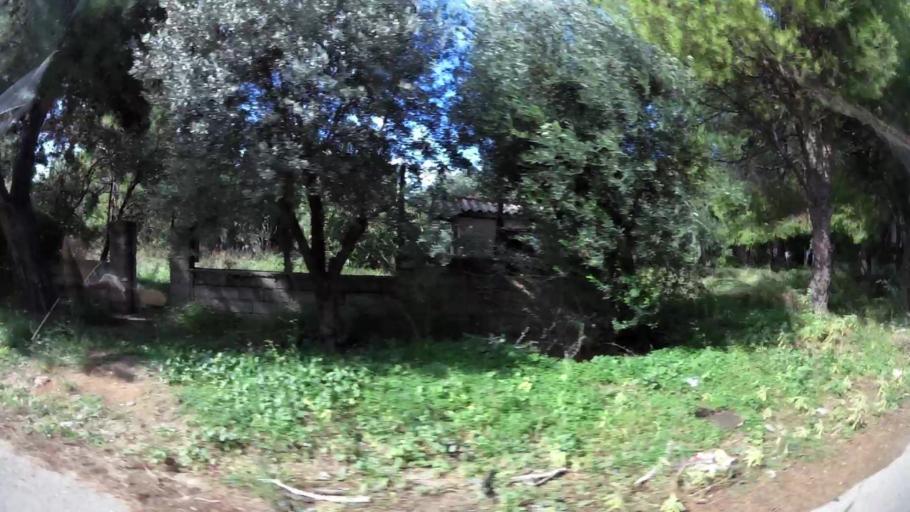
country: GR
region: Attica
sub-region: Nomarchia Anatolikis Attikis
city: Thrakomakedones
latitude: 38.1104
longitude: 23.7608
